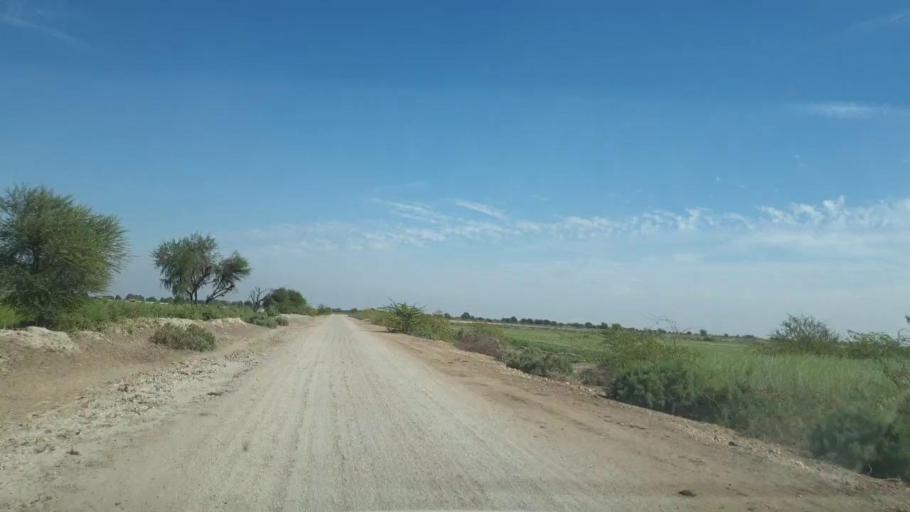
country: PK
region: Sindh
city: Pithoro
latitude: 25.5772
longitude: 69.3017
